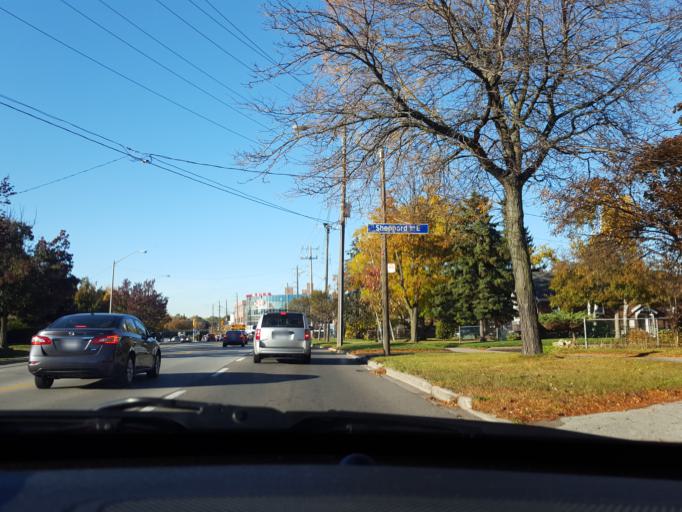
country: CA
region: Ontario
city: Scarborough
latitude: 43.7860
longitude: -79.2673
